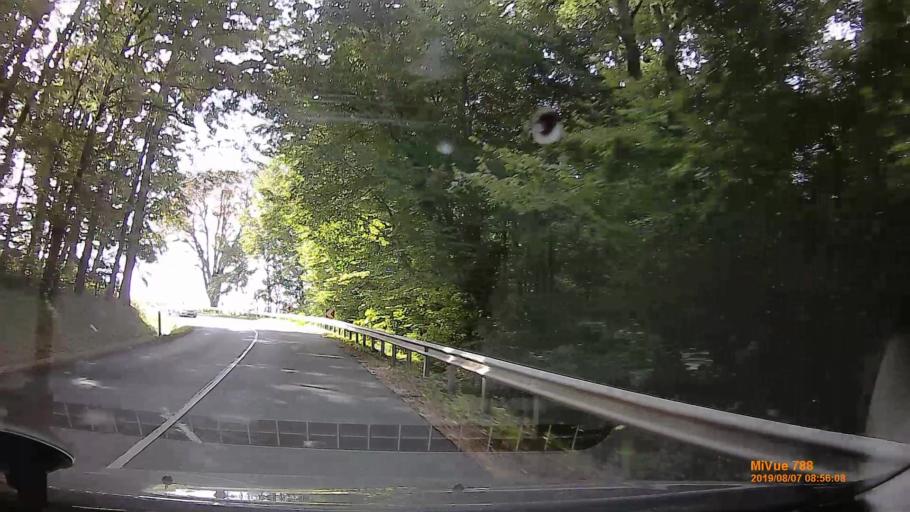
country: HU
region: Zala
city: Zalaegerszeg
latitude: 46.7316
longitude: 16.8858
